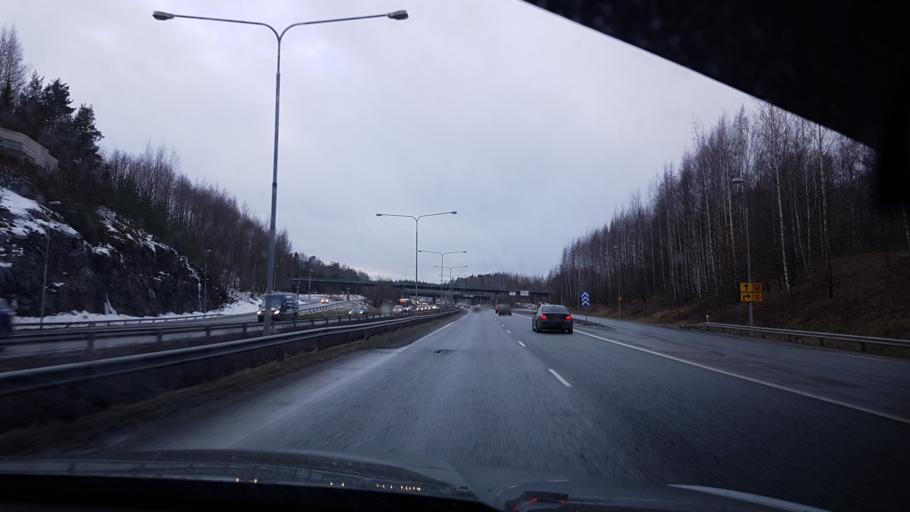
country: FI
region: Pirkanmaa
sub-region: Tampere
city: Tampere
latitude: 61.4700
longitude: 23.8505
